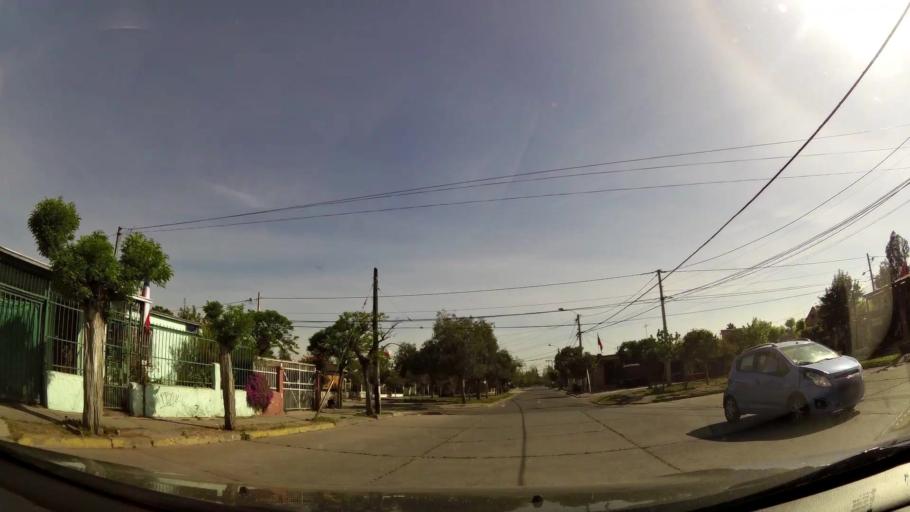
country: CL
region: Santiago Metropolitan
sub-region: Provincia de Cordillera
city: Puente Alto
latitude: -33.6067
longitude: -70.5887
